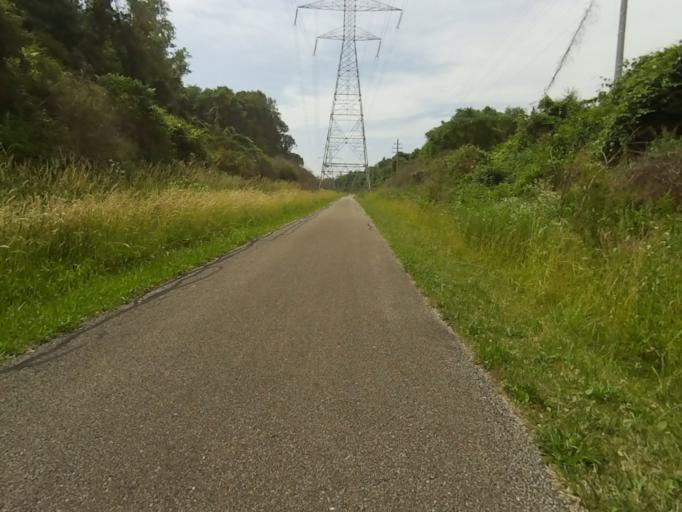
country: US
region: Ohio
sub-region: Cuyahoga County
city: Walton Hills
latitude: 41.3264
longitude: -81.5695
